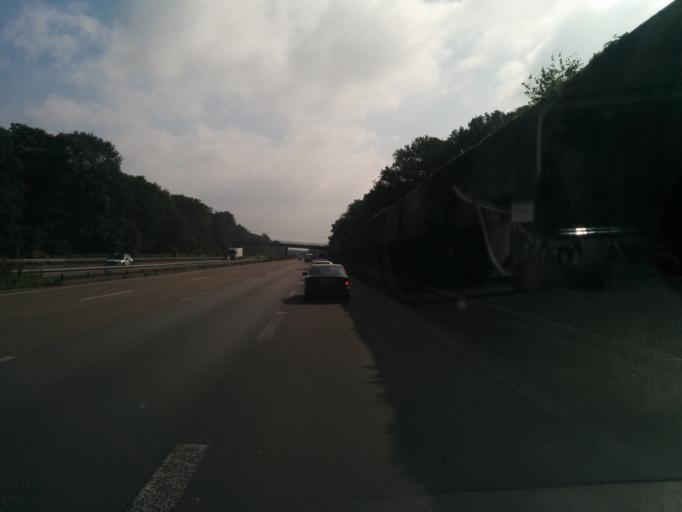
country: DE
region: North Rhine-Westphalia
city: Castrop-Rauxel
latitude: 51.5891
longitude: 7.3541
